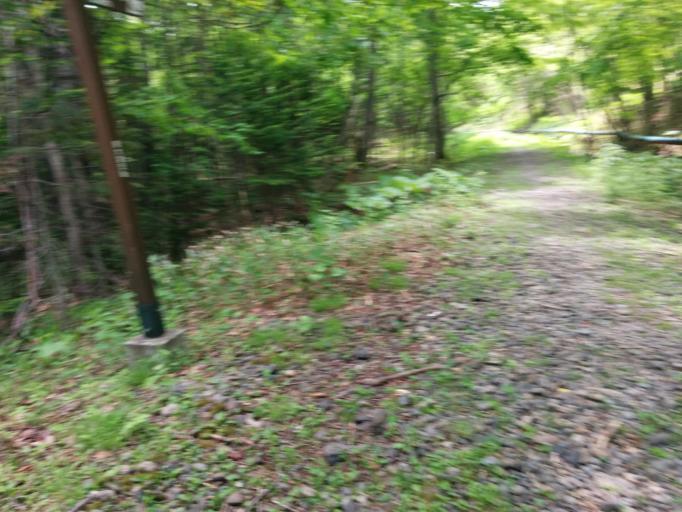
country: JP
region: Hokkaido
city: Otofuke
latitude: 43.3677
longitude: 143.1937
